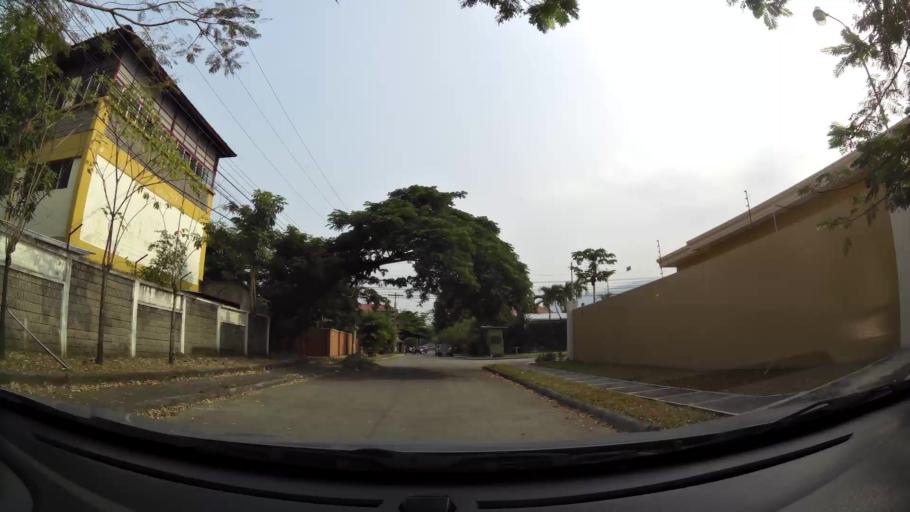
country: HN
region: Cortes
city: El Zapotal del Norte
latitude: 15.5103
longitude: -88.0398
